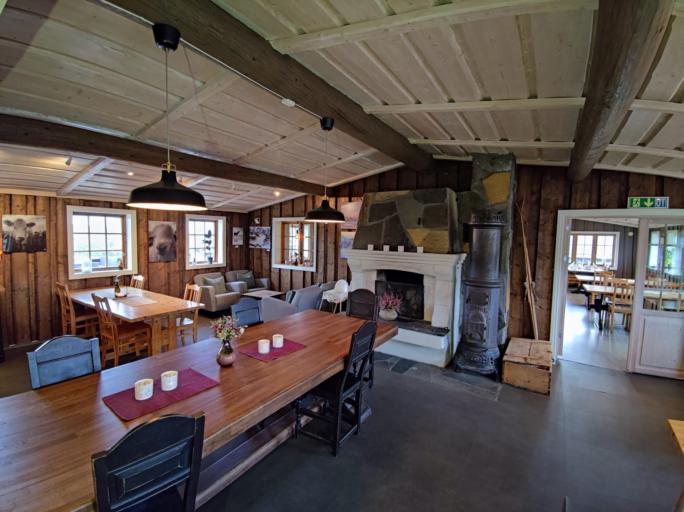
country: NO
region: Oppland
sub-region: Vang
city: Vang
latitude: 61.0900
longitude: 8.7388
